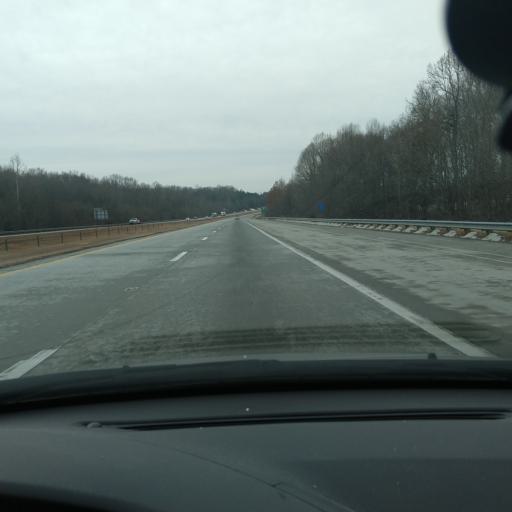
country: US
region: North Carolina
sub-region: Davidson County
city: Lexington
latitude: 35.8577
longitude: -80.2719
